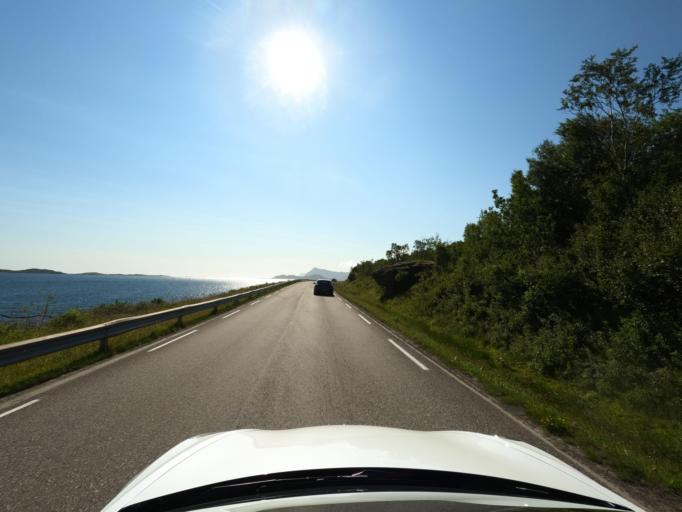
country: NO
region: Nordland
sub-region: Vagan
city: Kabelvag
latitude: 68.2605
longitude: 14.2340
